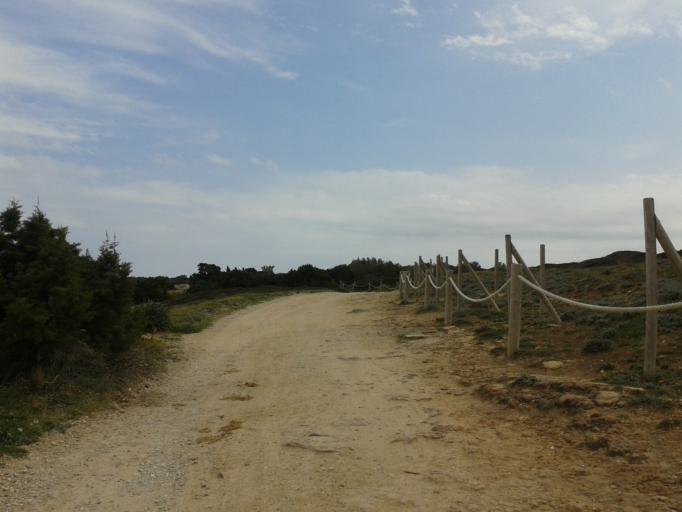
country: ES
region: Balearic Islands
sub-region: Illes Balears
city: Son Servera
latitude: 39.5855
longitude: 3.3903
